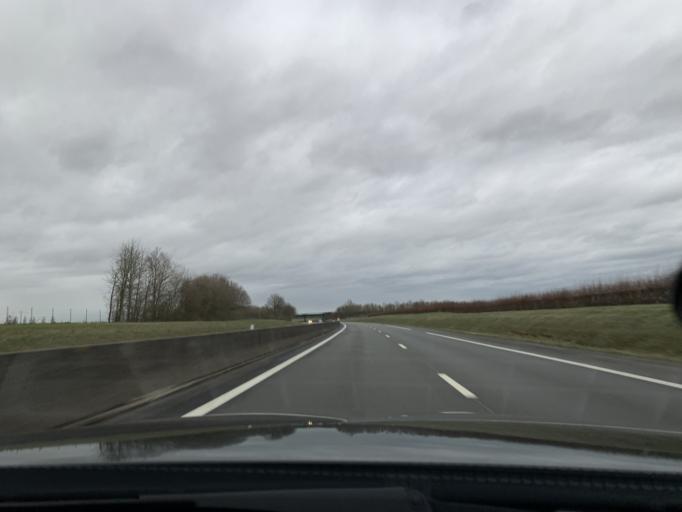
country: FR
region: Picardie
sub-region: Departement de l'Oise
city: Tille
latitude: 49.5111
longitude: 2.1830
